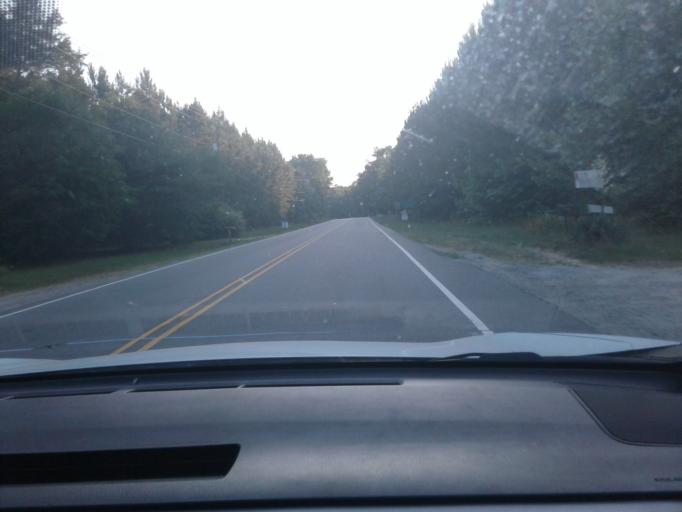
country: US
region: North Carolina
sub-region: Wake County
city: Fuquay-Varina
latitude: 35.5522
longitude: -78.8116
